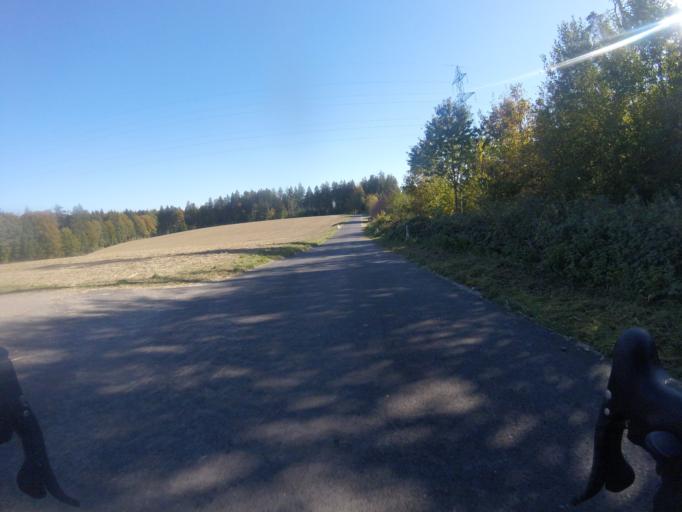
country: CH
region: Bern
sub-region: Bern-Mittelland District
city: Kirchlindach
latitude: 47.0111
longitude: 7.4060
